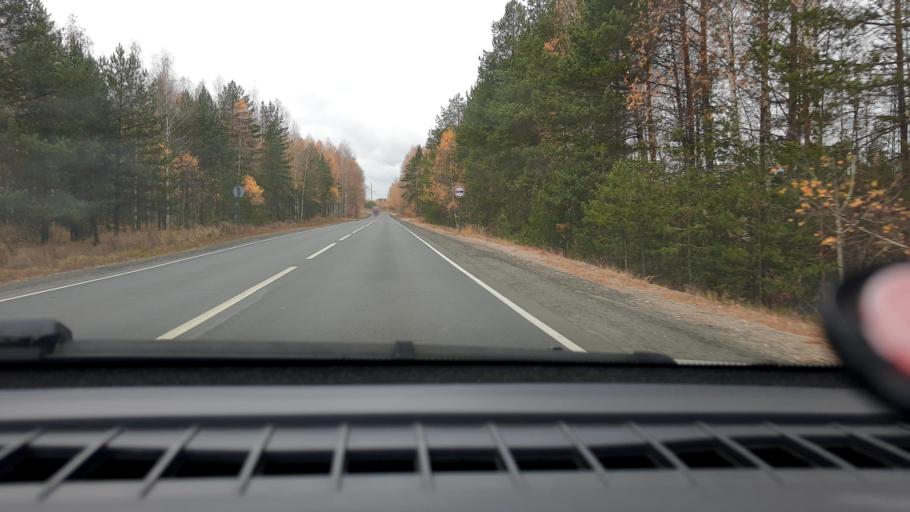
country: RU
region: Nizjnij Novgorod
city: Lukino
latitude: 56.3621
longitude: 43.6015
